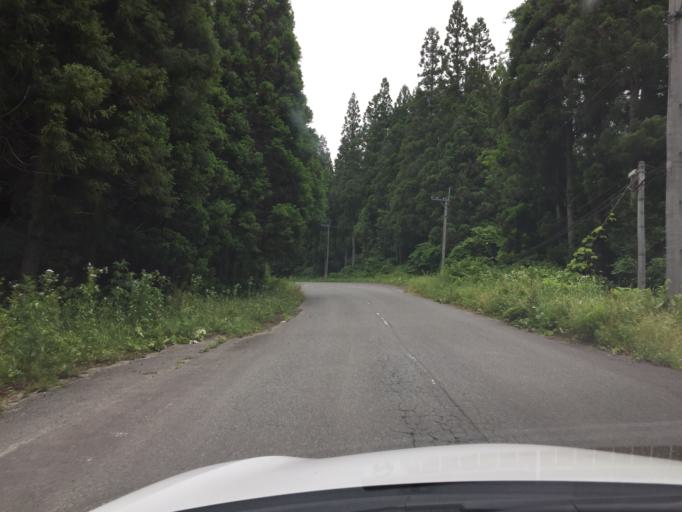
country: JP
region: Fukushima
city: Iwaki
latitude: 37.1707
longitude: 140.7118
